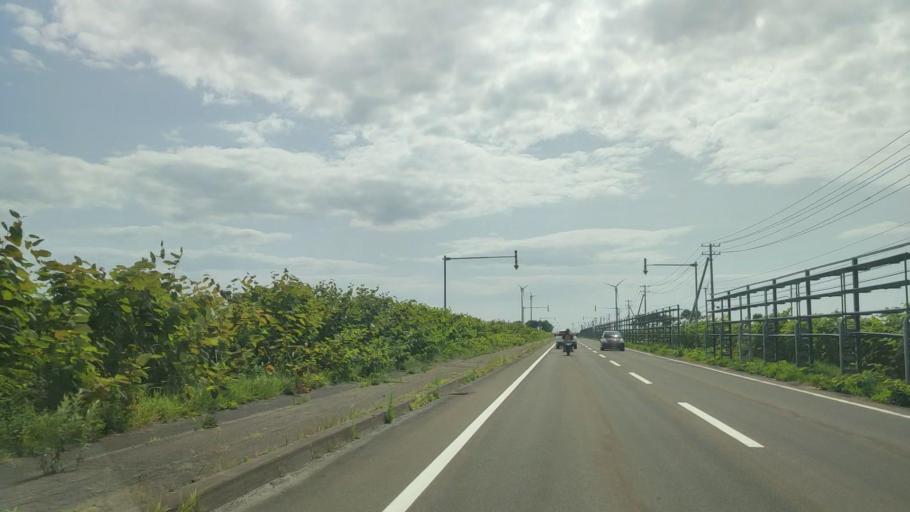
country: JP
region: Hokkaido
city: Rumoi
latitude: 44.3941
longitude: 141.7182
